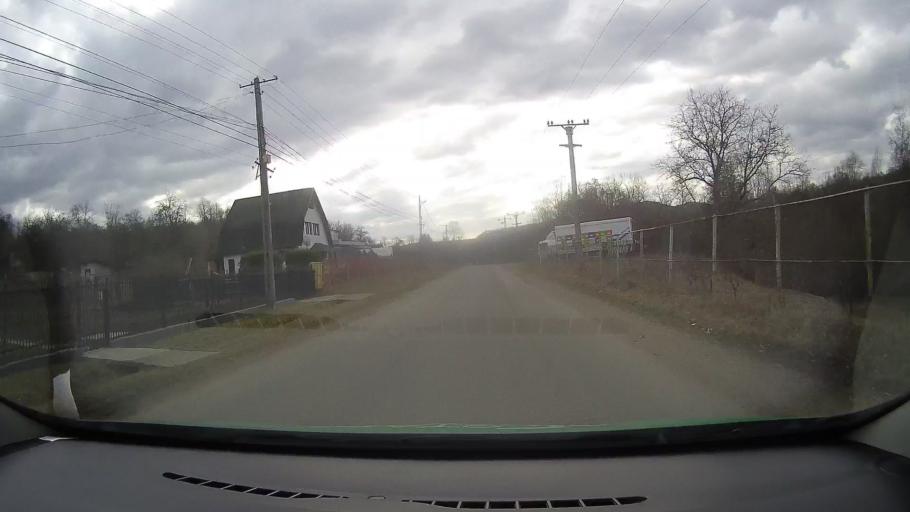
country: RO
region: Dambovita
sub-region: Comuna Valea Lunga
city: Valea Lunga-Cricov
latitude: 45.0744
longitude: 25.5769
